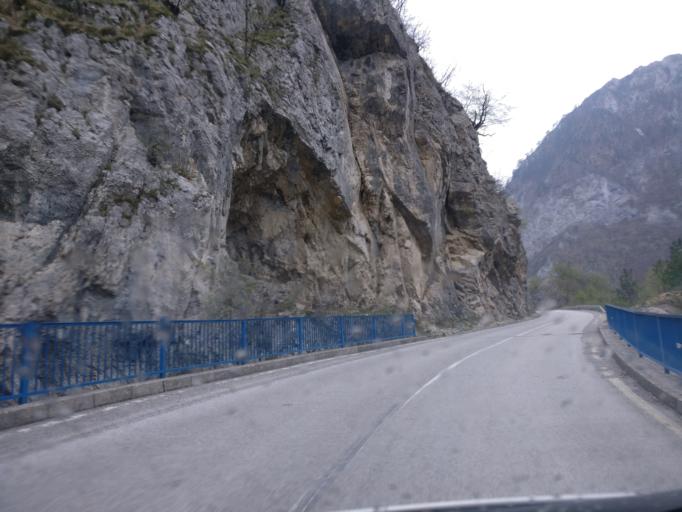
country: ME
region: Opstina Pluzine
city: Pluzine
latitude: 43.2242
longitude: 18.8474
